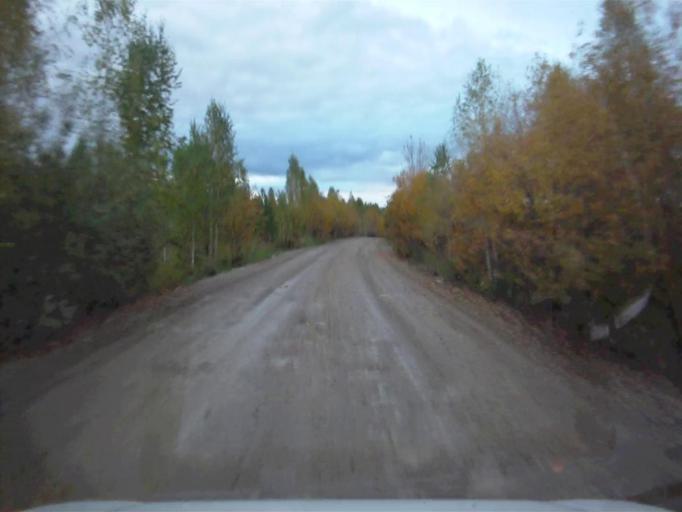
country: RU
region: Sverdlovsk
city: Mikhaylovsk
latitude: 56.2067
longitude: 59.2056
